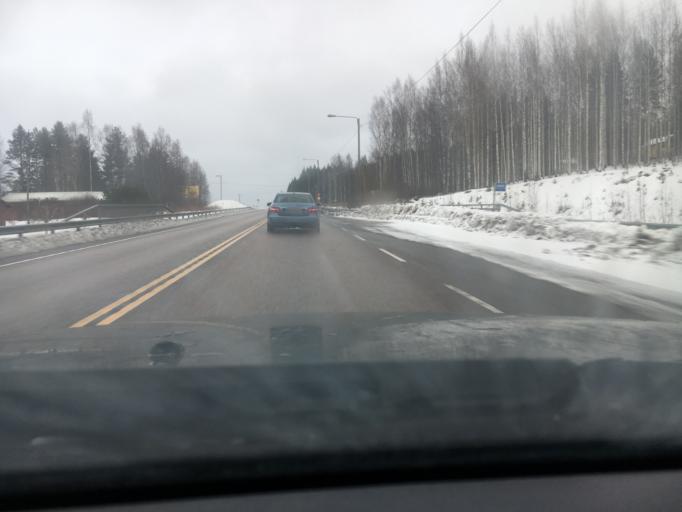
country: FI
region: Central Finland
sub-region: Joutsa
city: Leivonmaeki
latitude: 61.9182
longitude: 26.1169
